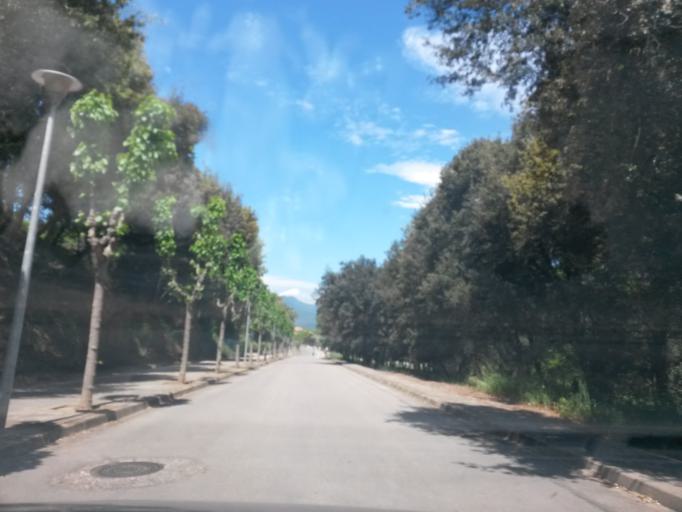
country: ES
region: Catalonia
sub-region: Provincia de Girona
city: Vilablareix
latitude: 41.9635
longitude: 2.7639
